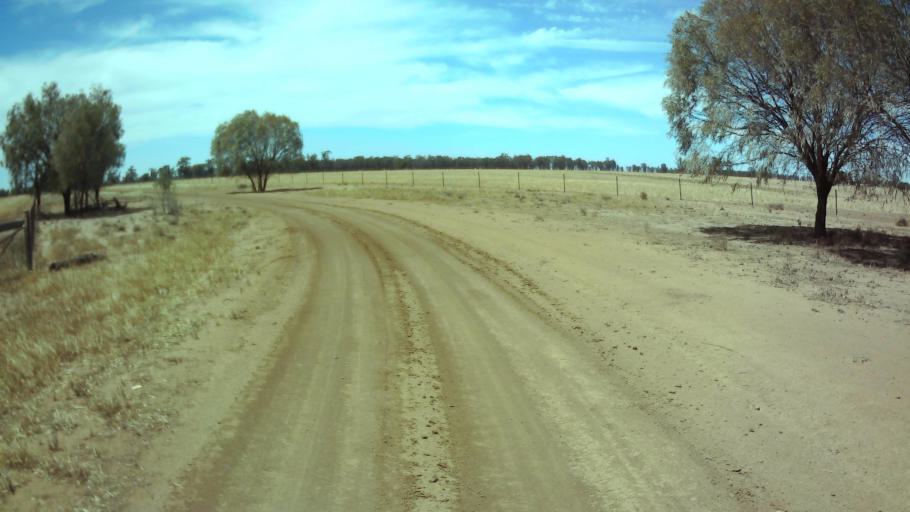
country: AU
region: New South Wales
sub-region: Weddin
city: Grenfell
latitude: -33.8958
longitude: 147.8017
